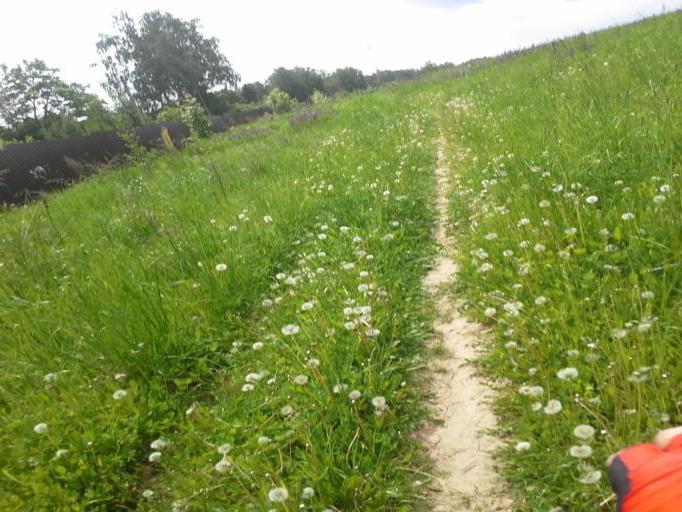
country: RU
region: Moskovskaya
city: Lesnoy Gorodok
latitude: 55.6492
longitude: 37.1893
